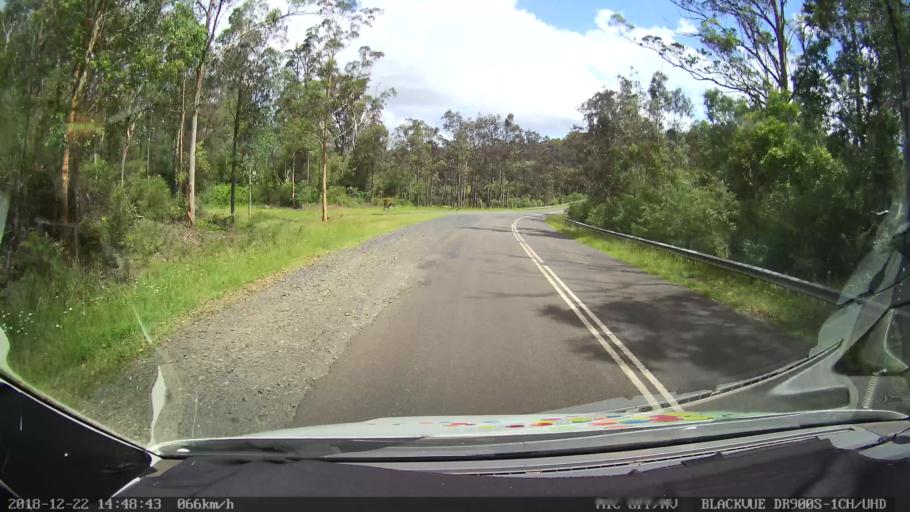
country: AU
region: New South Wales
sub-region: Bellingen
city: Dorrigo
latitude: -30.1829
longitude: 152.5516
